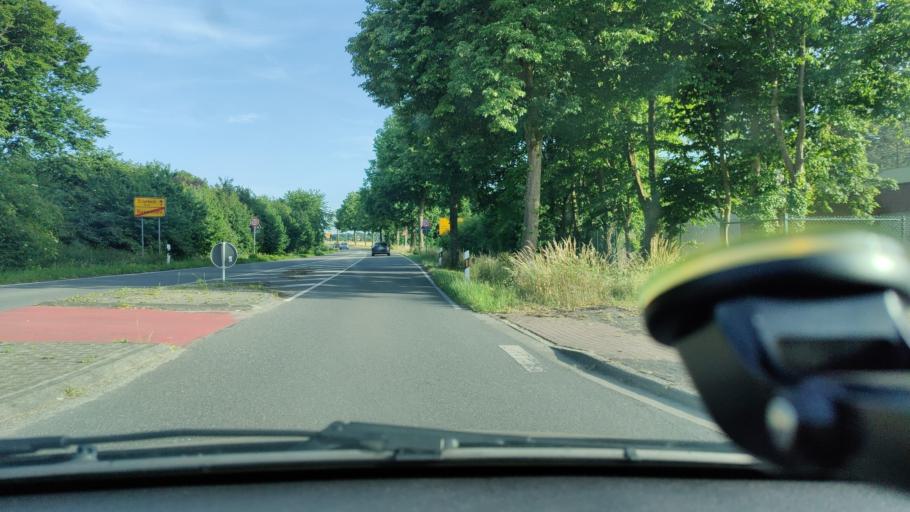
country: DE
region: North Rhine-Westphalia
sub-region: Regierungsbezirk Munster
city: Schoppingen
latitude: 52.0168
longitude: 7.2156
